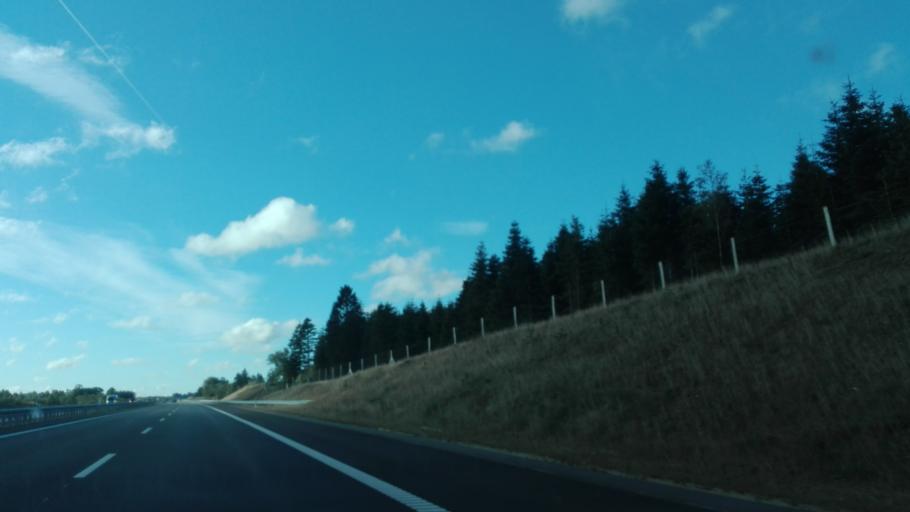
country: DK
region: Central Jutland
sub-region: Silkeborg Kommune
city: Silkeborg
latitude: 56.1739
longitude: 9.4767
